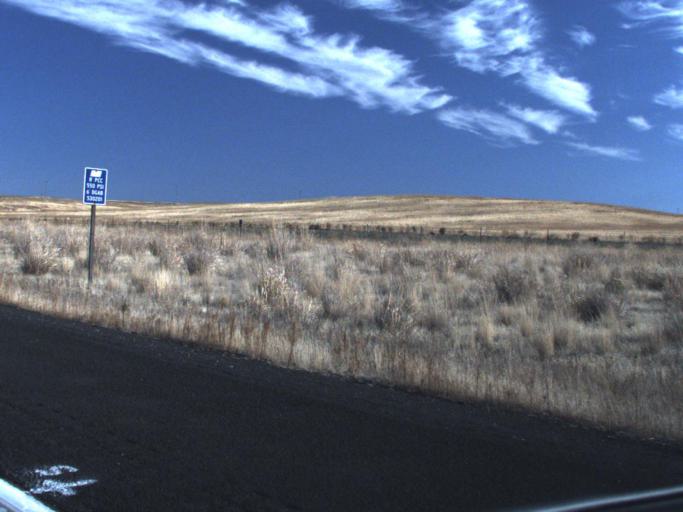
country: US
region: Washington
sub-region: Adams County
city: Ritzville
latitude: 47.0705
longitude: -118.4095
